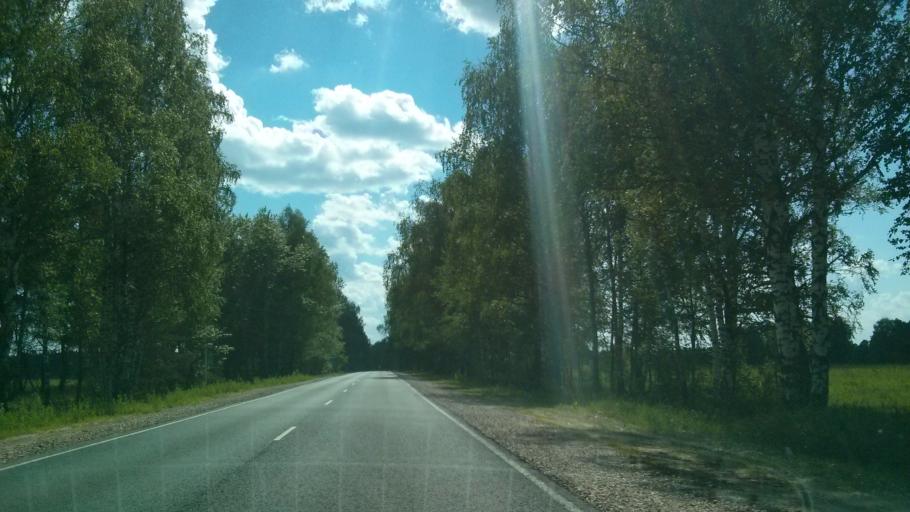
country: RU
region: Vladimir
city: Murom
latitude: 55.5184
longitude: 41.9330
